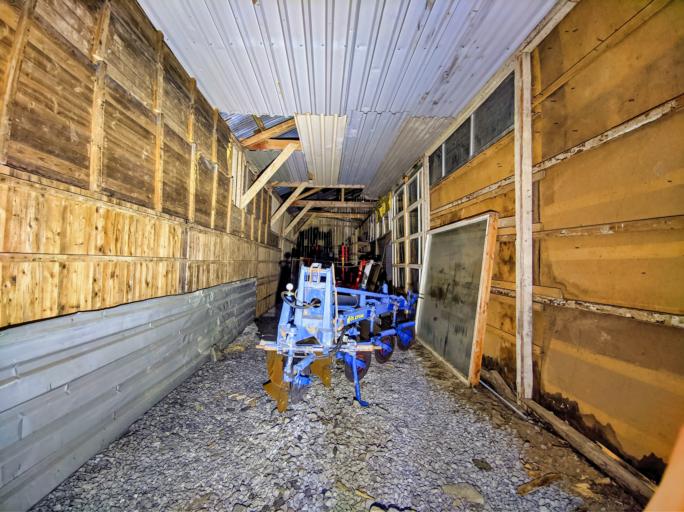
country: NO
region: Akershus
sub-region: Sorum
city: Sorumsand
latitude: 59.9554
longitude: 11.2150
